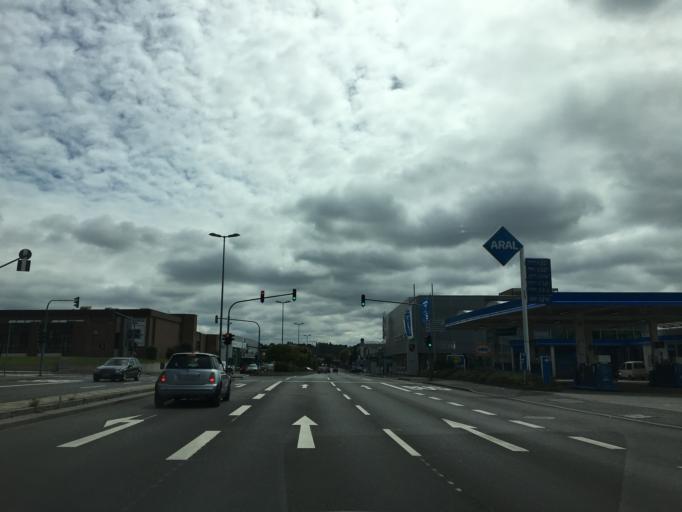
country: DE
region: Hesse
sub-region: Regierungsbezirk Darmstadt
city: Wiesbaden
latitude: 50.0625
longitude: 8.2527
